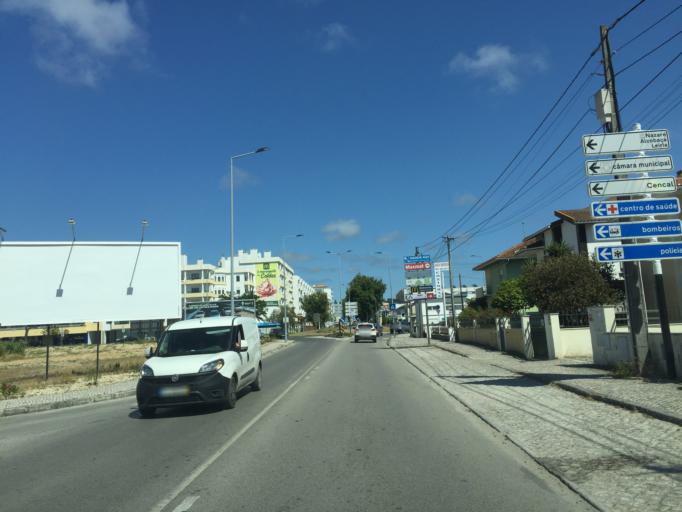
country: PT
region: Leiria
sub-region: Caldas da Rainha
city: Caldas da Rainha
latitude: 39.4050
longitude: -9.1485
